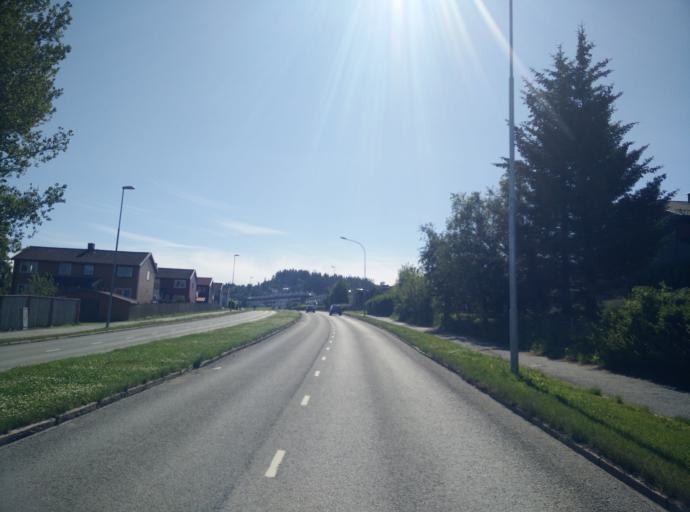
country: NO
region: Sor-Trondelag
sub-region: Trondheim
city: Trondheim
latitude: 63.4139
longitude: 10.3644
